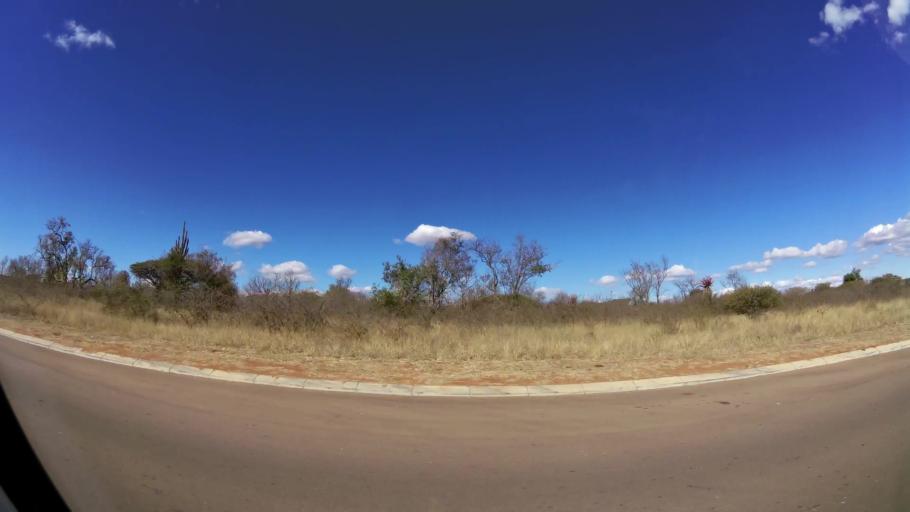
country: ZA
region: Limpopo
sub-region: Capricorn District Municipality
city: Polokwane
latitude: -23.8699
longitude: 29.4960
